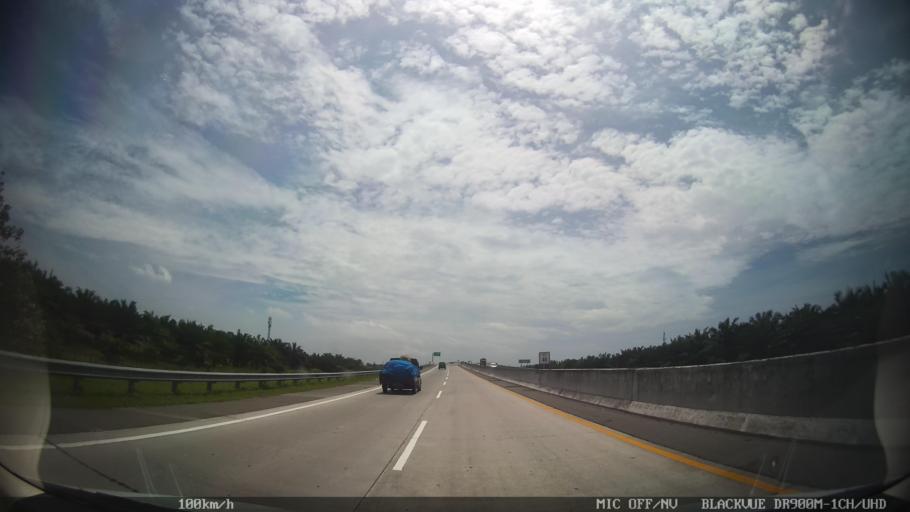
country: ID
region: North Sumatra
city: Perbaungan
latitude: 3.5316
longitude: 98.8826
